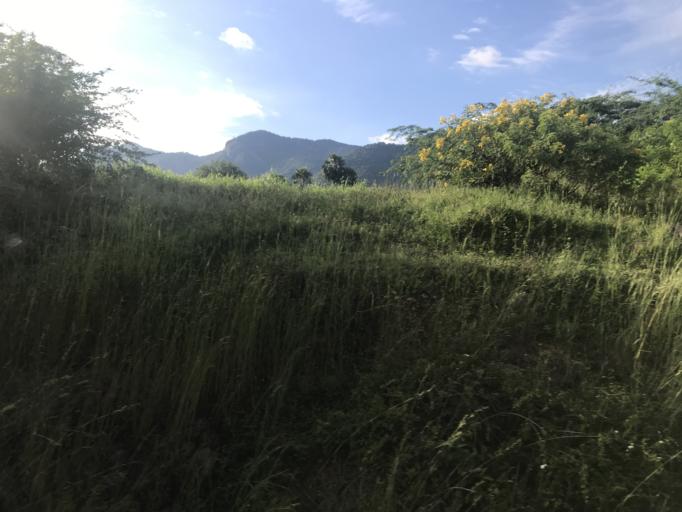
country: IN
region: Tamil Nadu
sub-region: Coimbatore
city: Madukkarai
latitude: 10.8905
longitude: 76.8805
